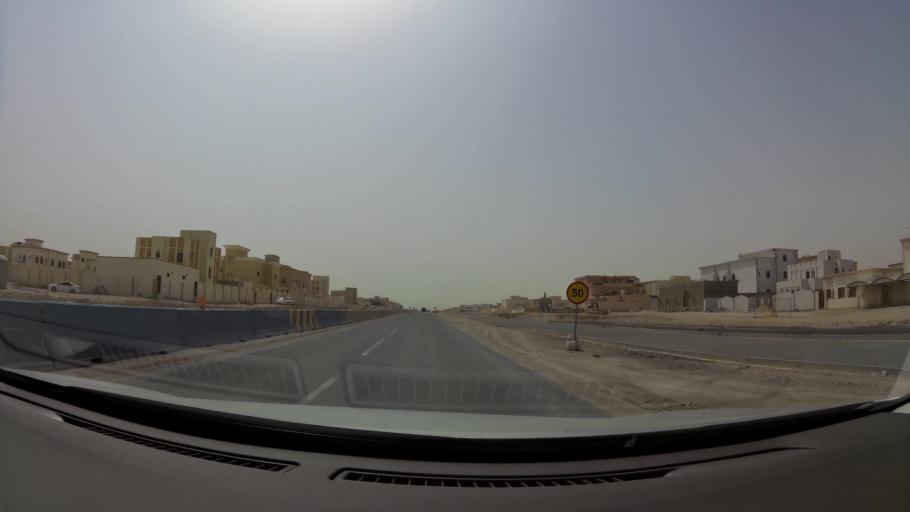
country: QA
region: Baladiyat ar Rayyan
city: Ar Rayyan
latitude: 25.2535
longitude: 51.3674
